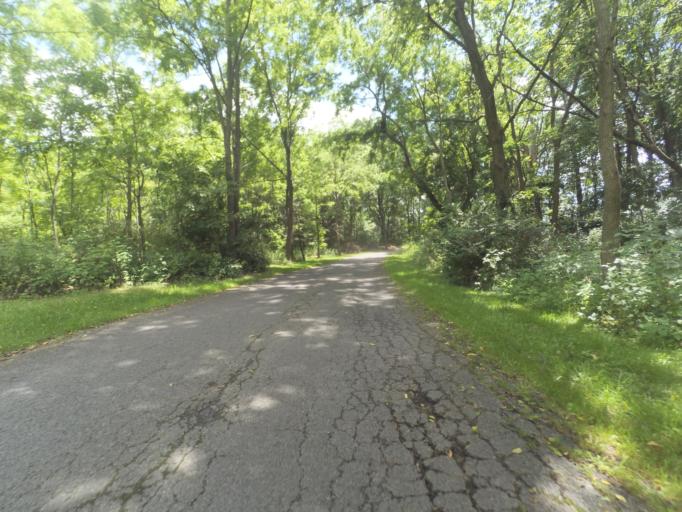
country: US
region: Pennsylvania
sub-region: Centre County
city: Lemont
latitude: 40.7848
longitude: -77.8173
